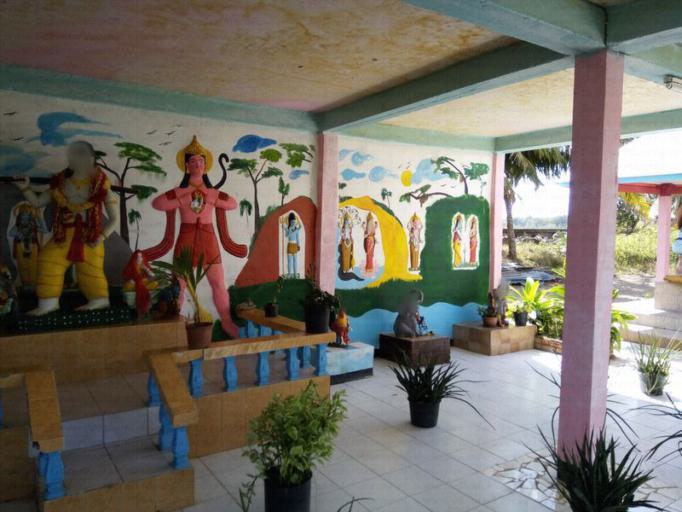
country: SR
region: Paramaribo
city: Paramaribo
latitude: 5.9043
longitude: -55.2260
